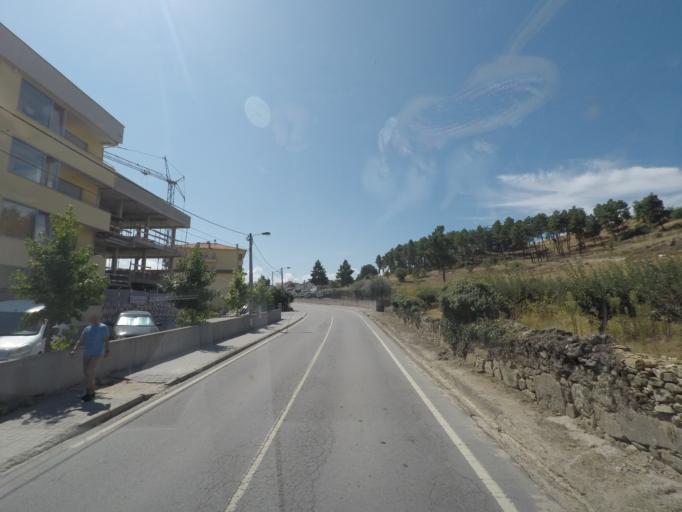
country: PT
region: Vila Real
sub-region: Sabrosa
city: Sabrosa
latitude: 41.2688
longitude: -7.4789
